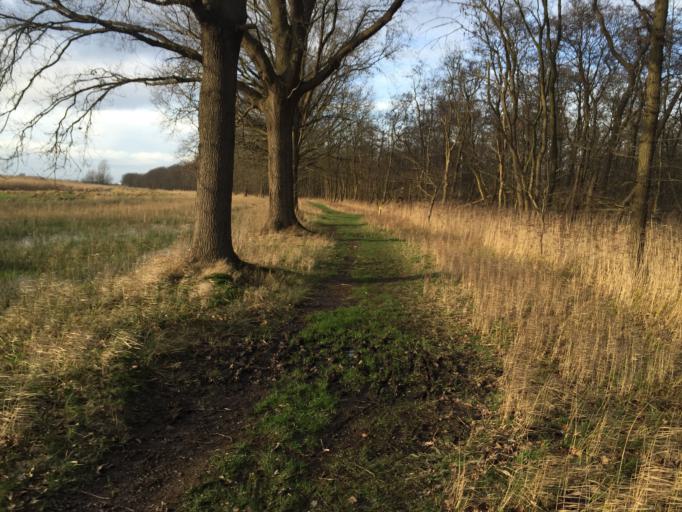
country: NL
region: North Holland
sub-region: Gemeente Bussum
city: Bussum
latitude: 52.2814
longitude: 5.1235
